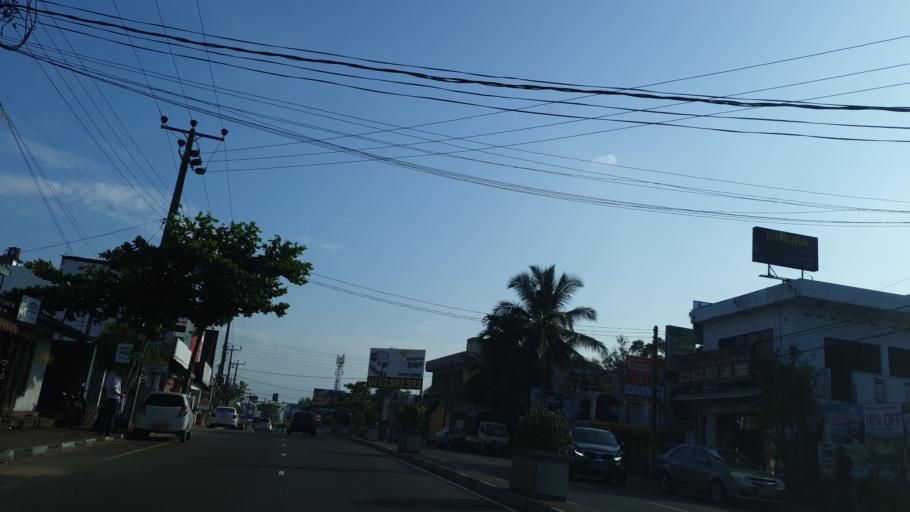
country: LK
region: Western
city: Battaramulla South
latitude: 6.8801
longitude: 79.9346
